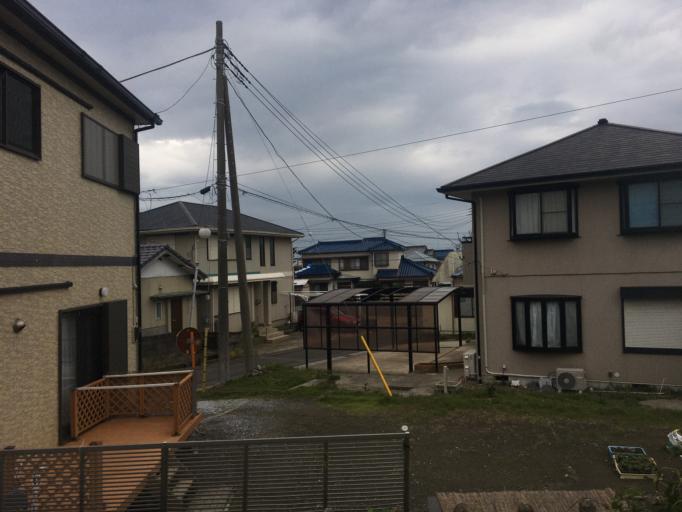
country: JP
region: Chiba
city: Tateyama
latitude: 35.1399
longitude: 139.8394
